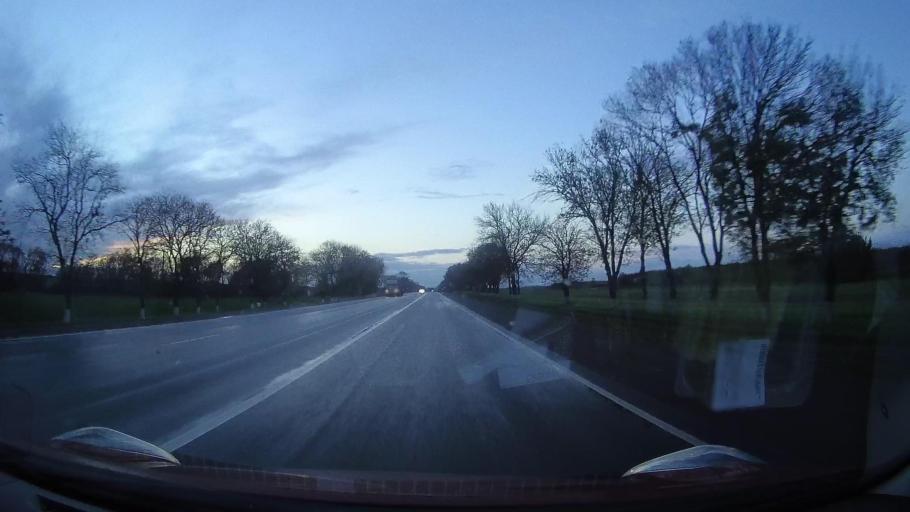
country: RU
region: Krasnodarskiy
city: Uspenskoye
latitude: 44.8215
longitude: 41.3612
